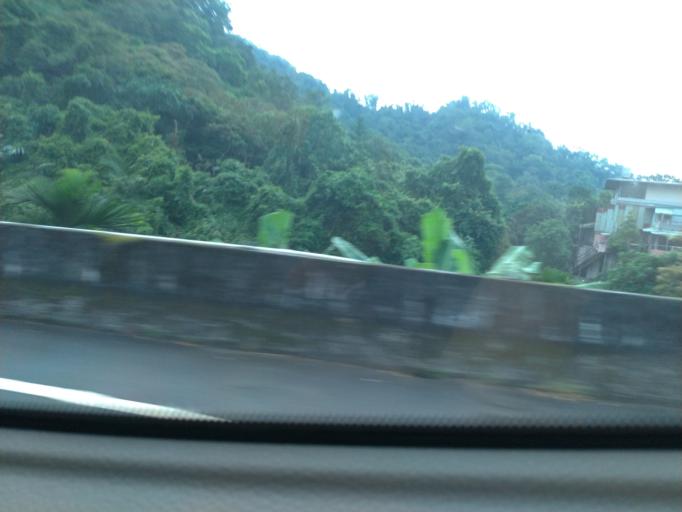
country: TW
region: Taipei
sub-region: Taipei
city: Banqiao
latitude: 24.9223
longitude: 121.4262
